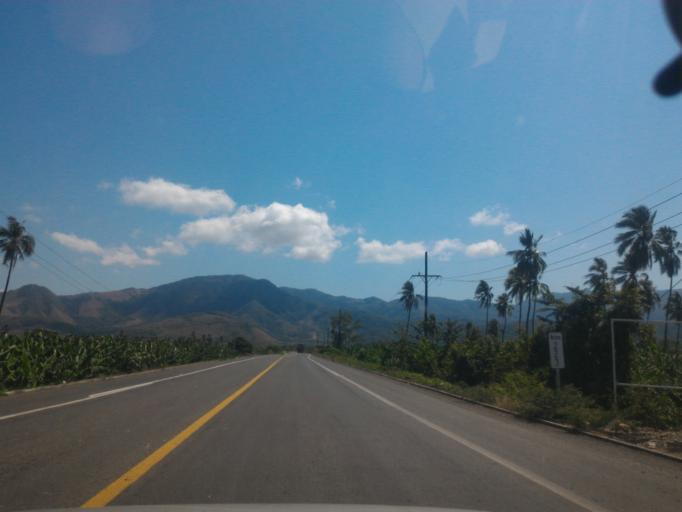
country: MX
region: Michoacan
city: Coahuayana Viejo
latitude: 18.6743
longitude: -103.6786
